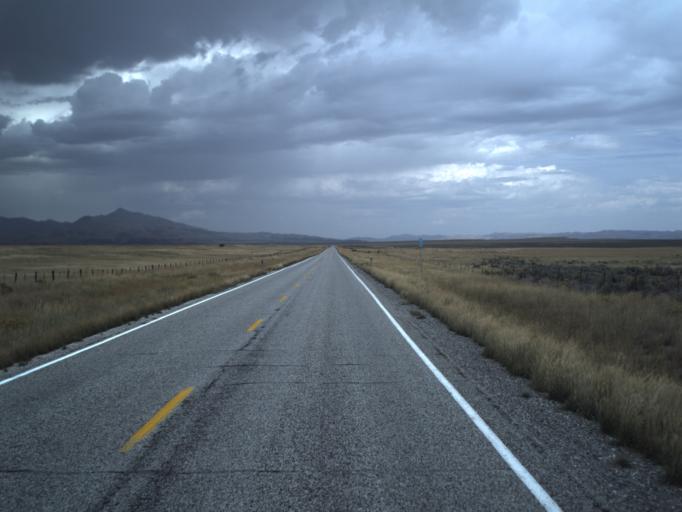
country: US
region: Idaho
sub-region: Oneida County
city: Malad City
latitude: 41.9187
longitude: -113.0963
